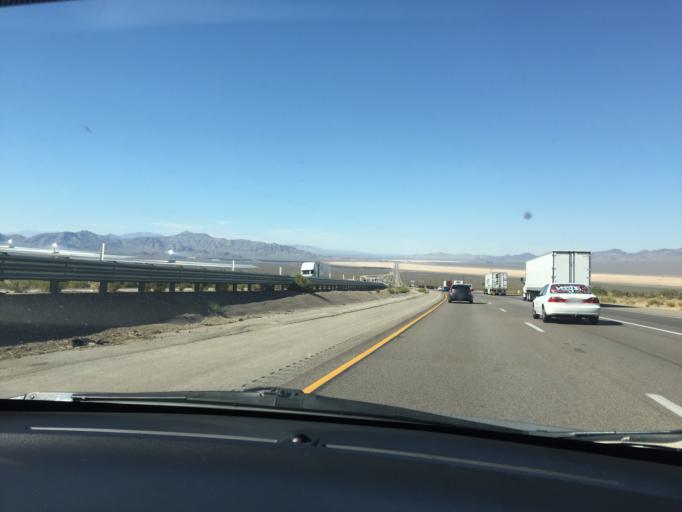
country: US
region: Nevada
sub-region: Clark County
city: Sandy Valley
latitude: 35.4737
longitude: -115.4486
